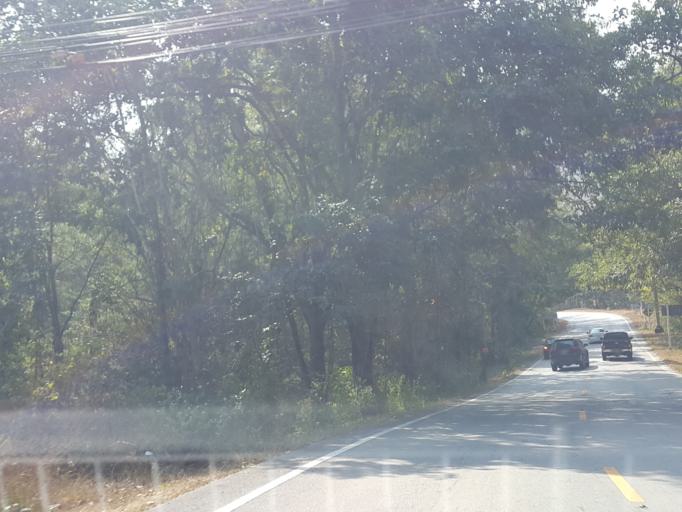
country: TH
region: Chiang Mai
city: Hot
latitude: 18.2223
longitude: 98.4450
